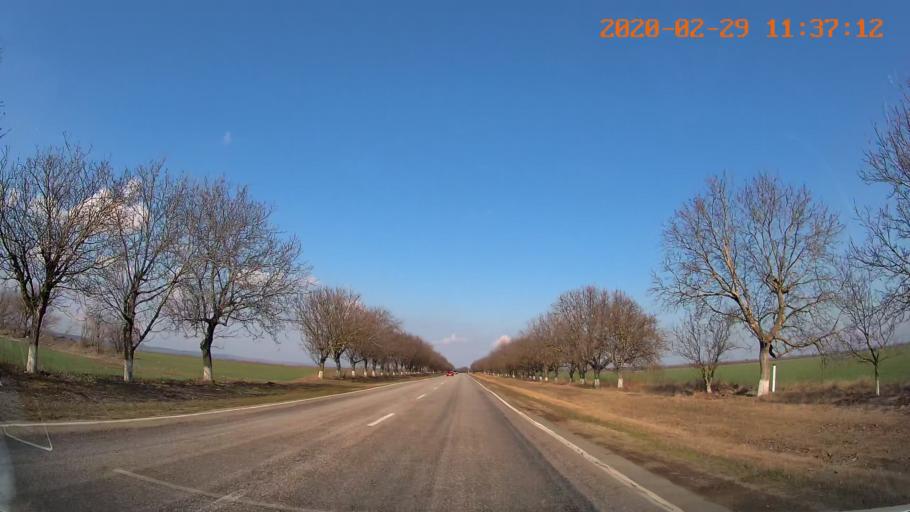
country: MD
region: Rezina
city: Saharna
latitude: 47.6081
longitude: 29.0482
